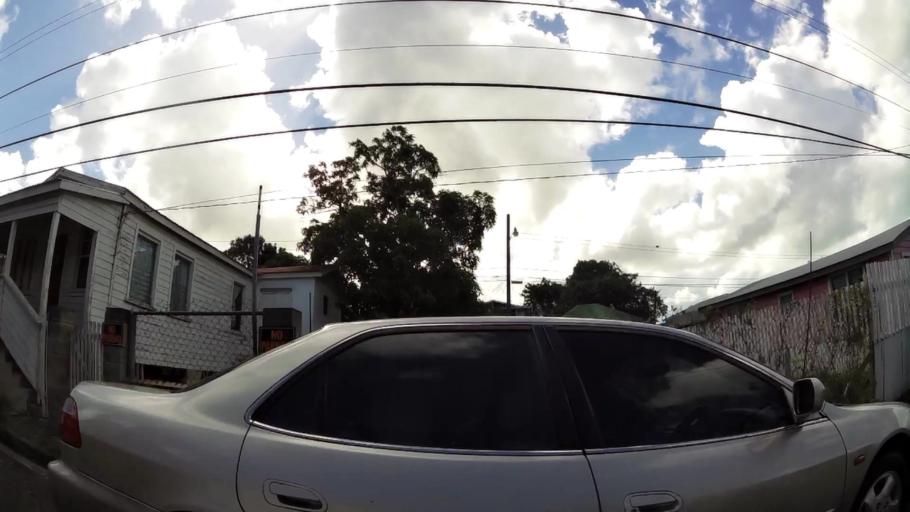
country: AG
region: Saint John
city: Saint John's
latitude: 17.1181
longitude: -61.8413
